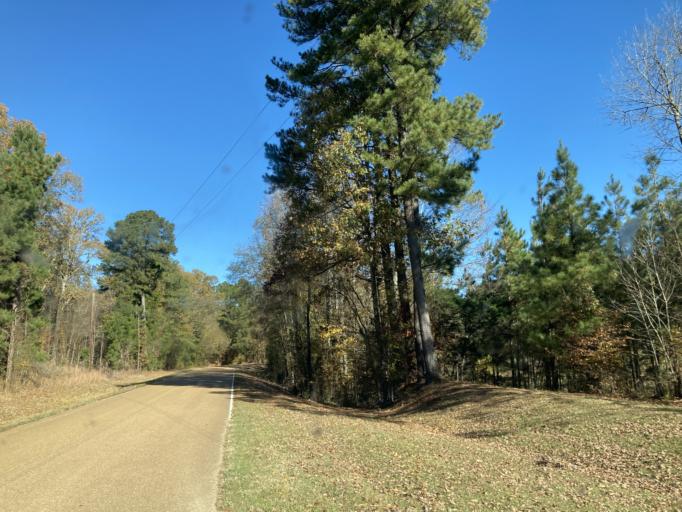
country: US
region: Mississippi
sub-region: Hinds County
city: Lynchburg
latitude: 32.6201
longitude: -90.5241
